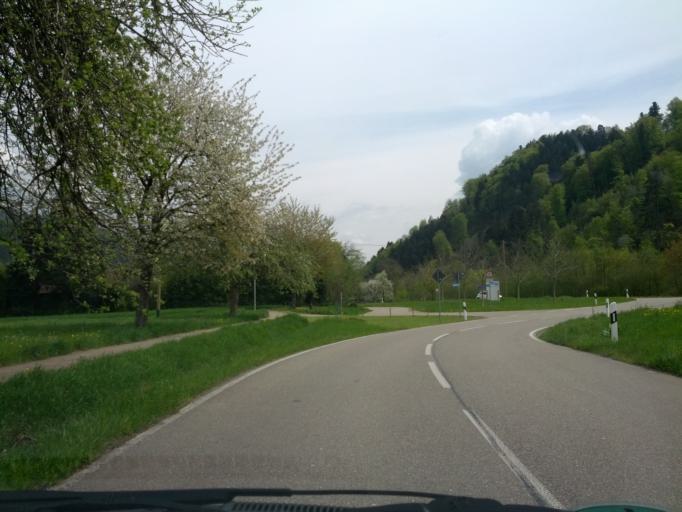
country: DE
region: Baden-Wuerttemberg
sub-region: Freiburg Region
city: Gutach im Breisgau
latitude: 48.1204
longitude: 8.0137
